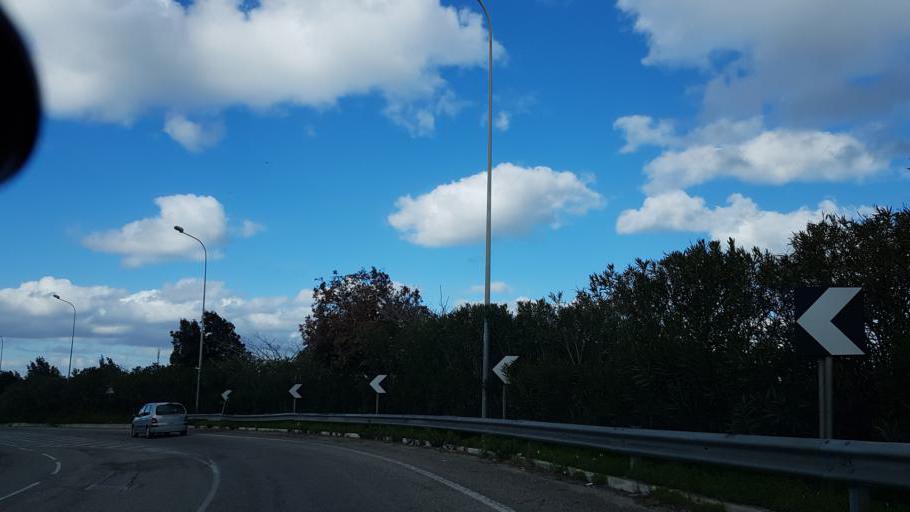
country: IT
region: Apulia
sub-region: Provincia di Brindisi
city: Brindisi
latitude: 40.6371
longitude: 17.9207
